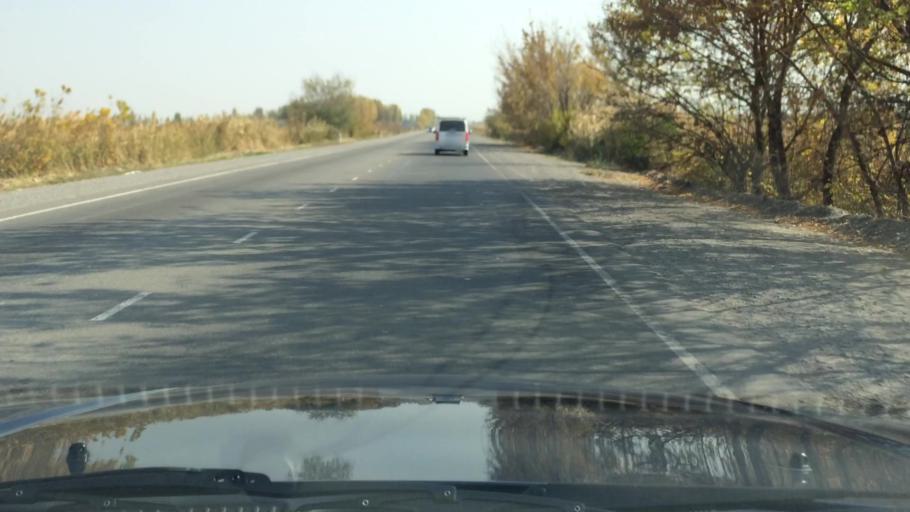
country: KG
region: Chuy
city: Lebedinovka
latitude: 42.9202
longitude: 74.7292
